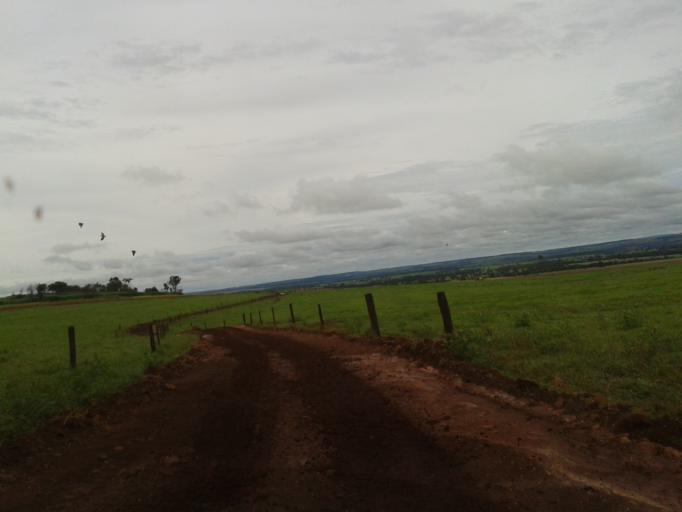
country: BR
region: Minas Gerais
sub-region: Capinopolis
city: Capinopolis
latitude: -18.7567
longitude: -49.7794
